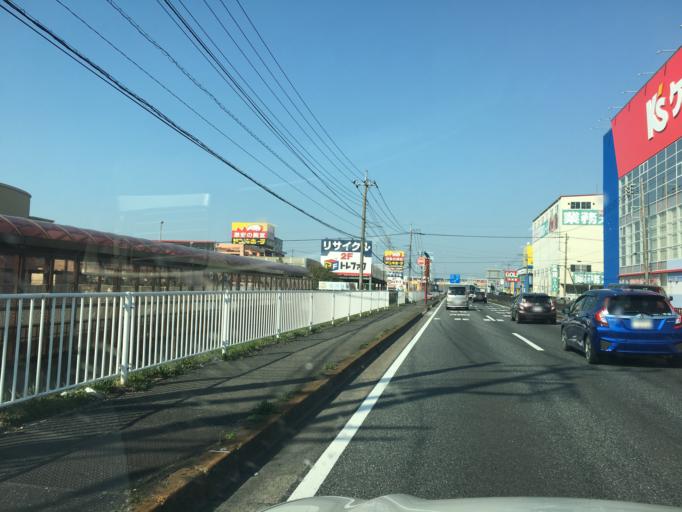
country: JP
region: Saitama
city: Kawagoe
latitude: 35.9167
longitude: 139.5009
